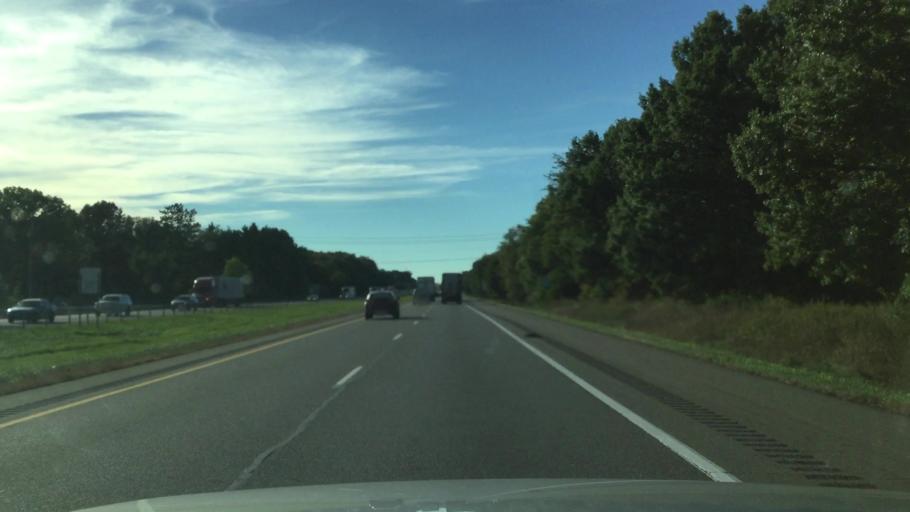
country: US
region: Michigan
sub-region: Calhoun County
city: Lakeview
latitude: 42.2631
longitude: -85.2063
